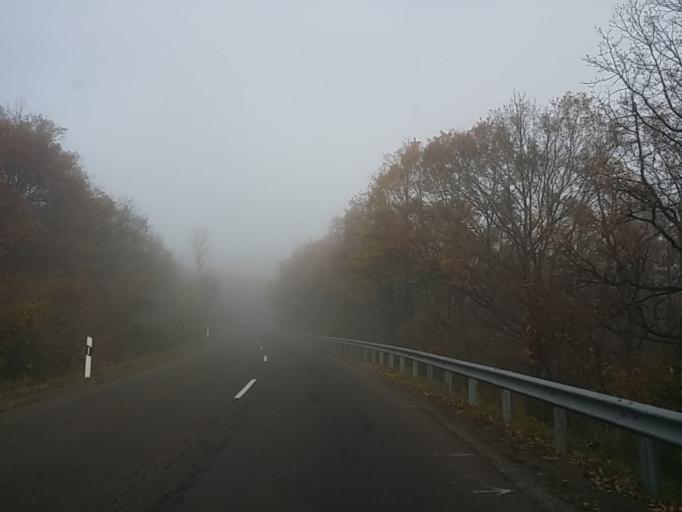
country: HU
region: Heves
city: Gyongyossolymos
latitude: 47.8369
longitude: 19.9635
